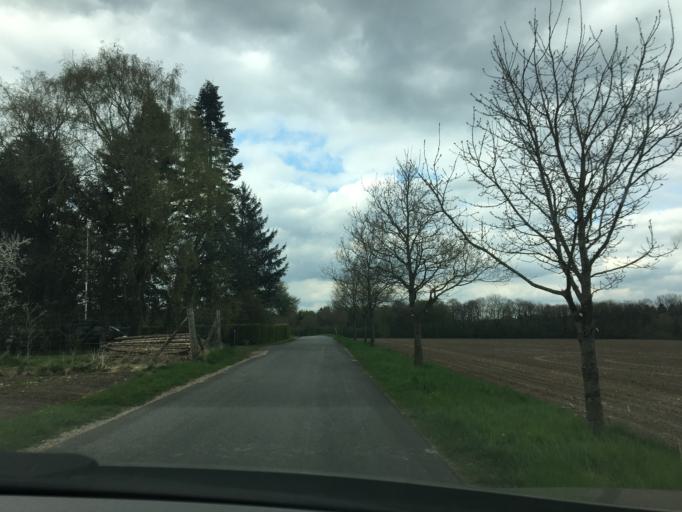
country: DK
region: Central Jutland
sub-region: Horsens Kommune
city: Braedstrup
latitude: 55.9643
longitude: 9.6879
